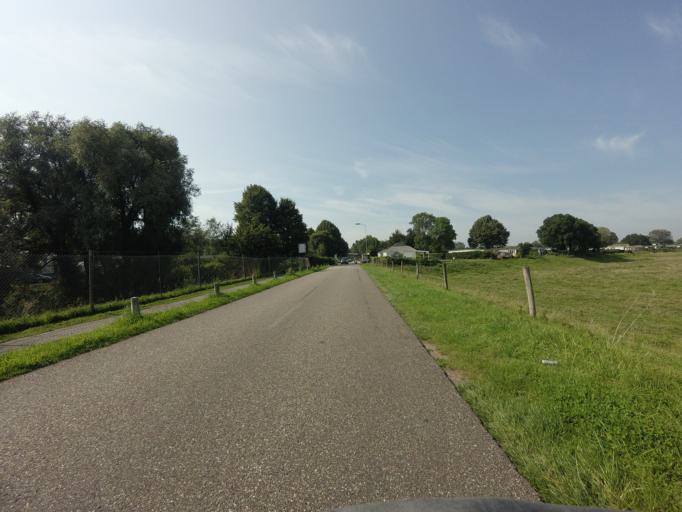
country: NL
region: Gelderland
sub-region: Gemeente Rheden
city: Rheden
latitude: 51.9954
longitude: 6.0312
